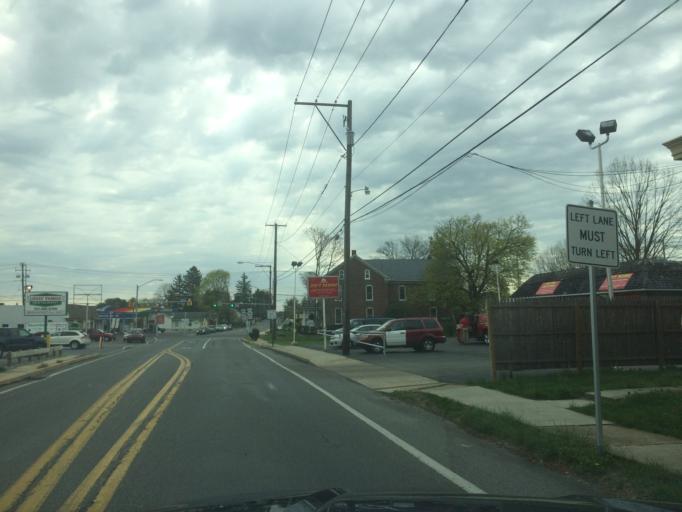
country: US
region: Pennsylvania
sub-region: Lancaster County
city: East Petersburg
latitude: 40.0531
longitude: -76.3612
